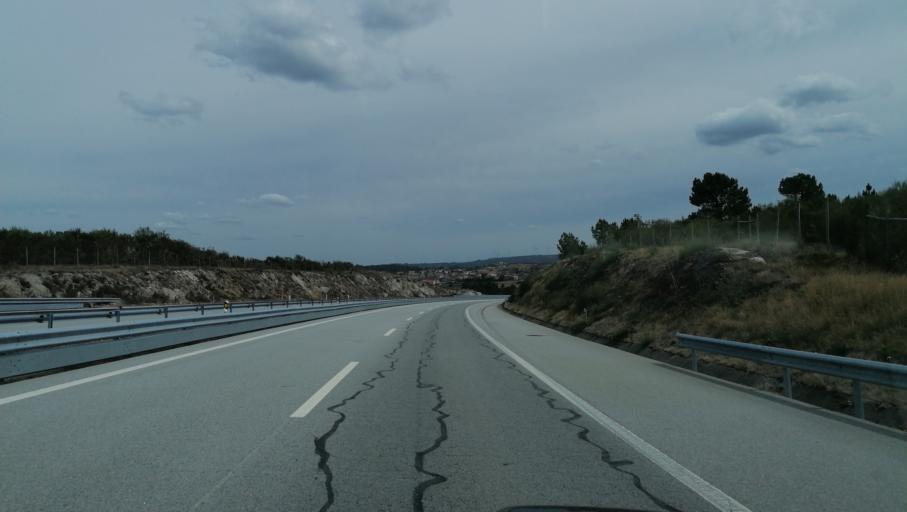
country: PT
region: Vila Real
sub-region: Vila Pouca de Aguiar
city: Vila Pouca de Aguiar
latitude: 41.5020
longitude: -7.7107
